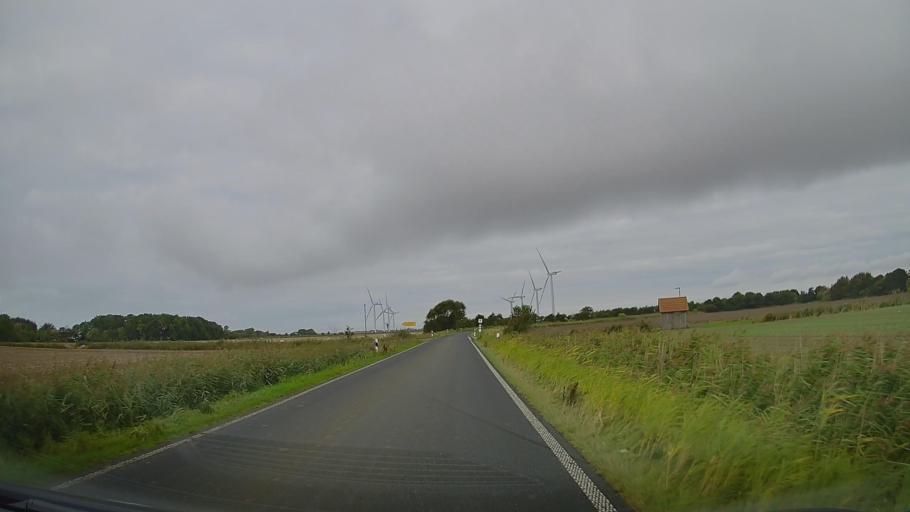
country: DE
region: Schleswig-Holstein
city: Galmsbull
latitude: 54.7676
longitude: 8.7168
